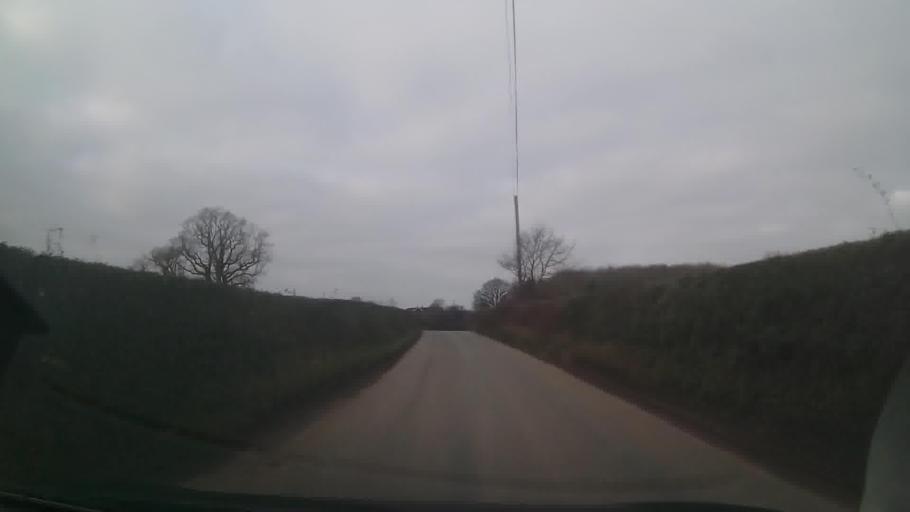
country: GB
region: England
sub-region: Shropshire
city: Bicton
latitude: 52.7712
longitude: -2.8425
